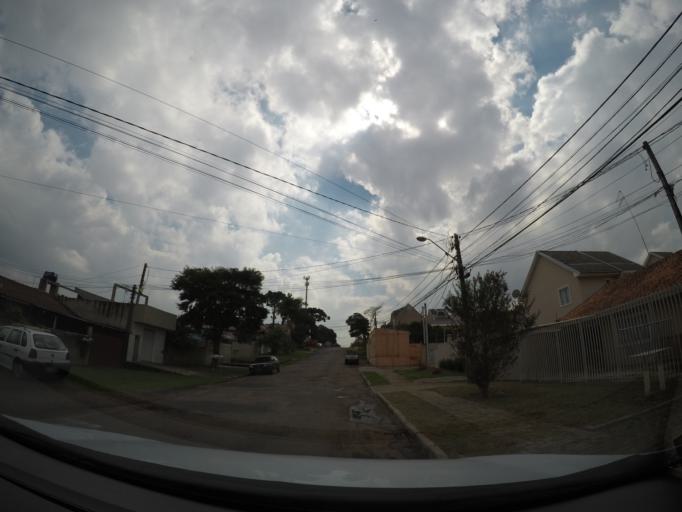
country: BR
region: Parana
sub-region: Sao Jose Dos Pinhais
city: Sao Jose dos Pinhais
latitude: -25.4895
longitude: -49.2531
